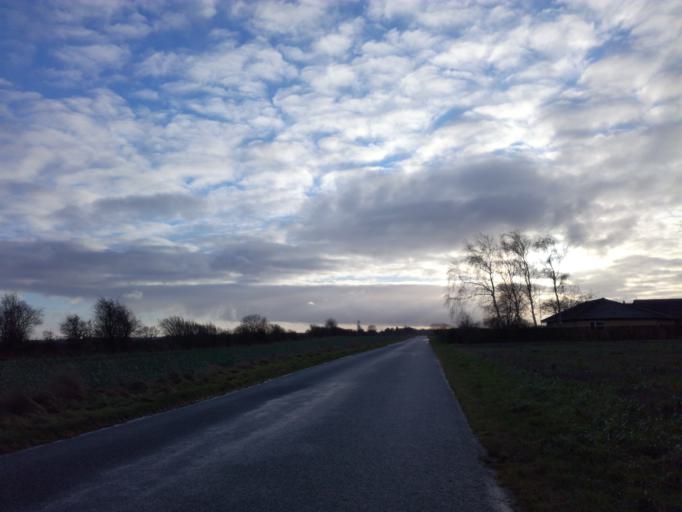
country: DK
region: South Denmark
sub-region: Fredericia Kommune
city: Taulov
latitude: 55.5652
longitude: 9.6037
